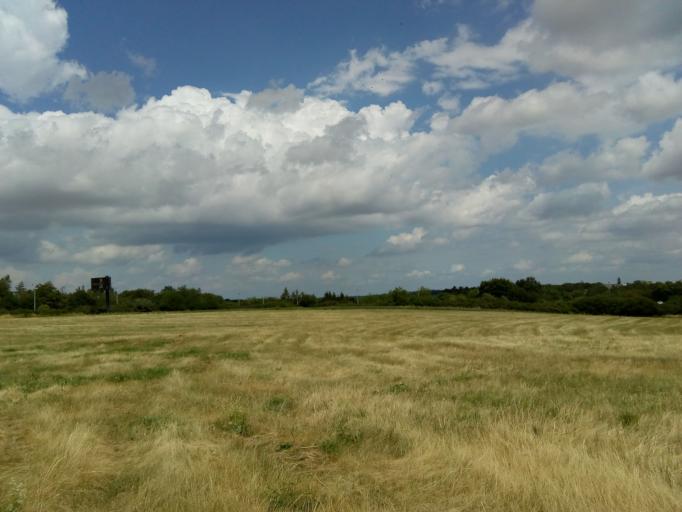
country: CZ
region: Central Bohemia
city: Tuchomerice
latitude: 50.1119
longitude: 14.2842
